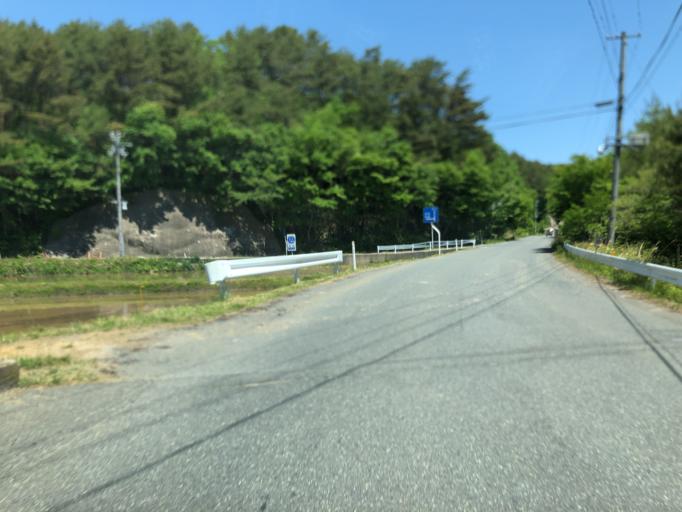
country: JP
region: Fukushima
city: Funehikimachi-funehiki
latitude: 37.5216
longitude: 140.7782
